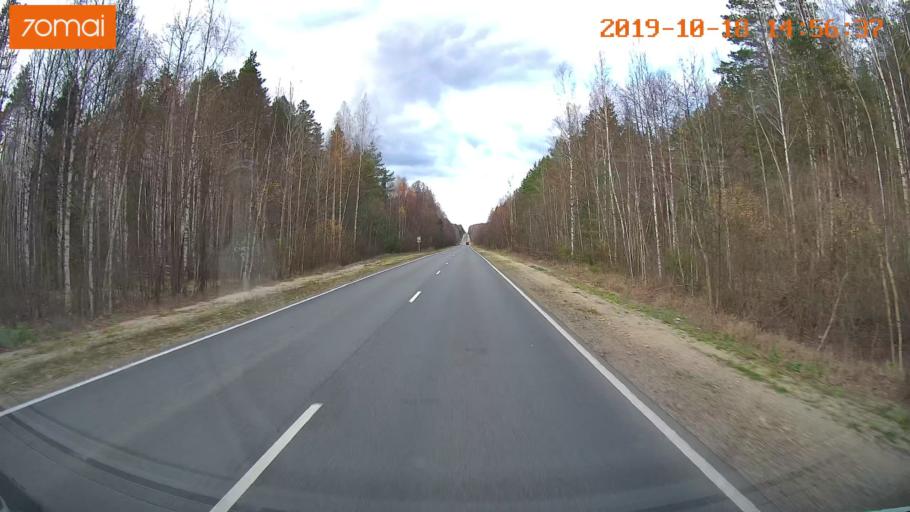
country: RU
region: Vladimir
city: Kurlovo
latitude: 55.4674
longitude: 40.5864
